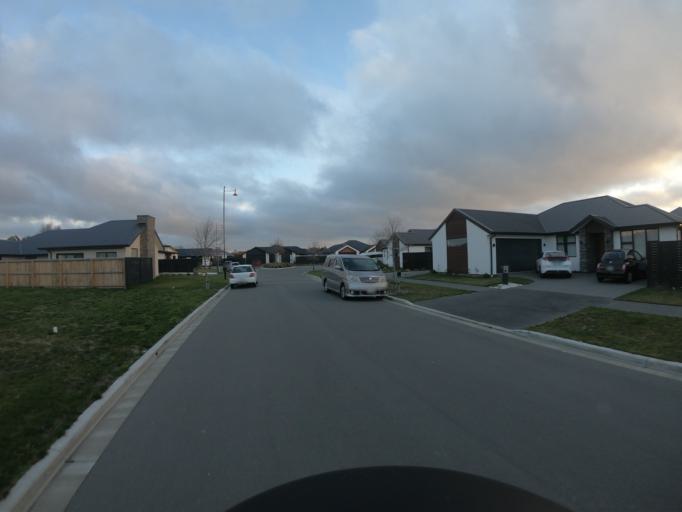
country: NZ
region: Canterbury
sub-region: Selwyn District
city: Prebbleton
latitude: -43.5660
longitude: 172.5596
